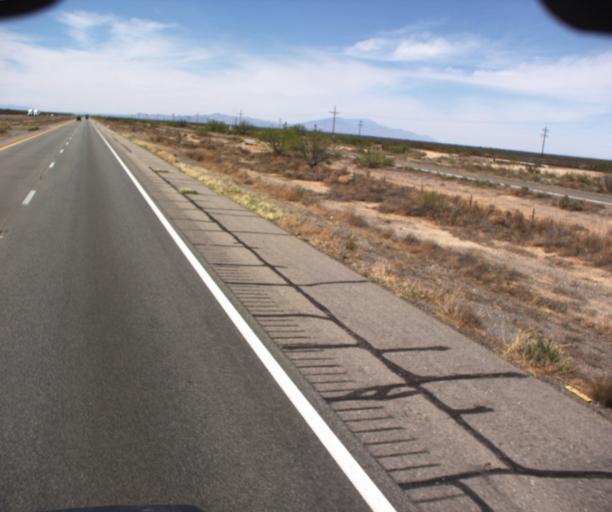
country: US
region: Arizona
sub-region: Cochise County
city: Willcox
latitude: 32.2858
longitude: -109.3027
